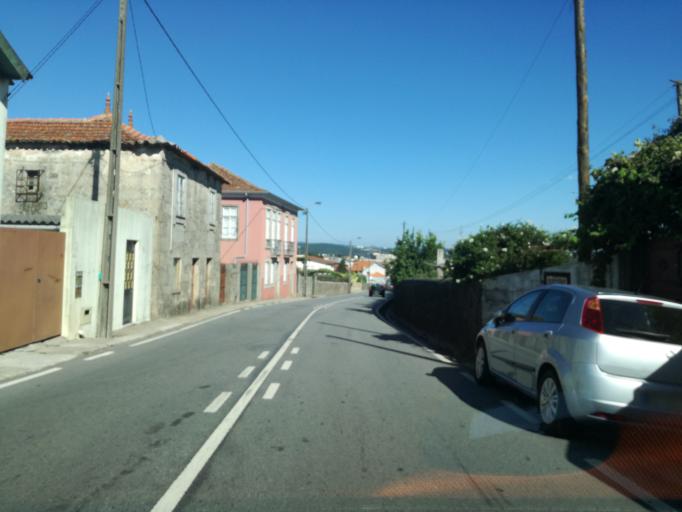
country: PT
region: Porto
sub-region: Trofa
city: Sao Romao do Coronado
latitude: 41.2840
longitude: -8.5772
